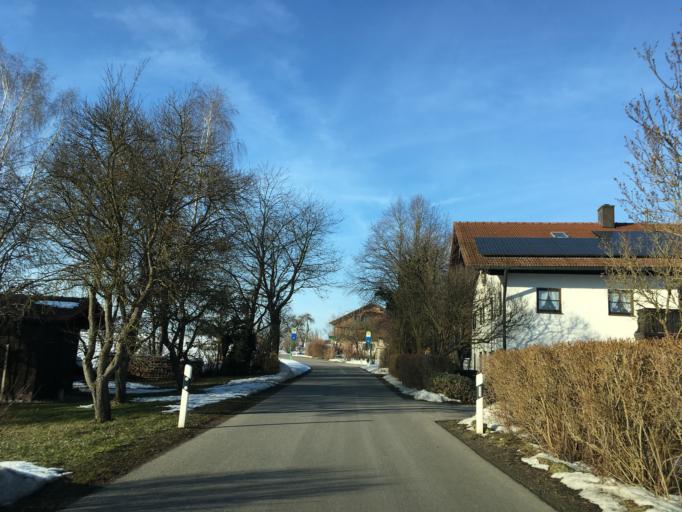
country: DE
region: Bavaria
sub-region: Upper Bavaria
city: Steinhoring
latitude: 48.1053
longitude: 12.0620
